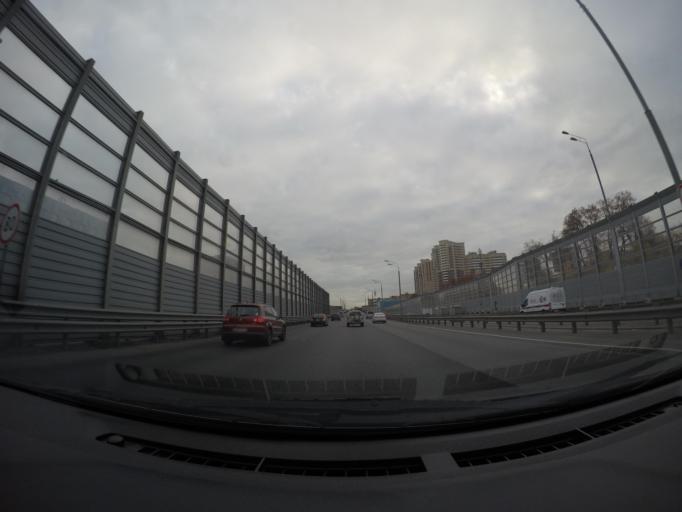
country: RU
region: Moskovskaya
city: Saltykovka
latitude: 55.7938
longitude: 37.9267
